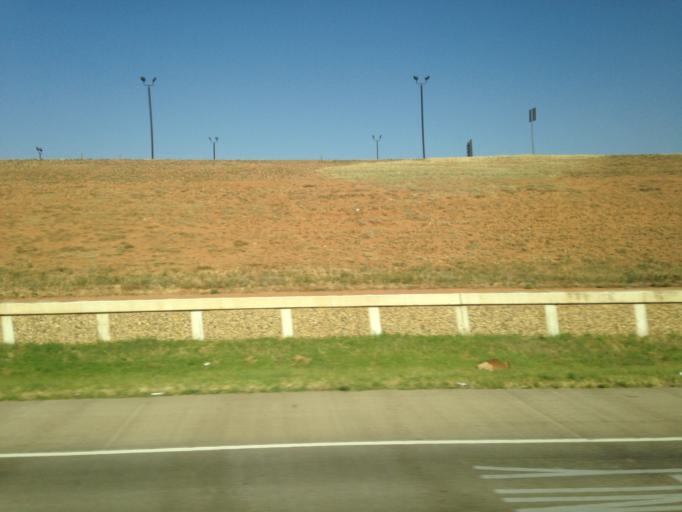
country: US
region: Texas
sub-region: Lubbock County
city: Lubbock
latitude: 33.5505
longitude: -101.8451
